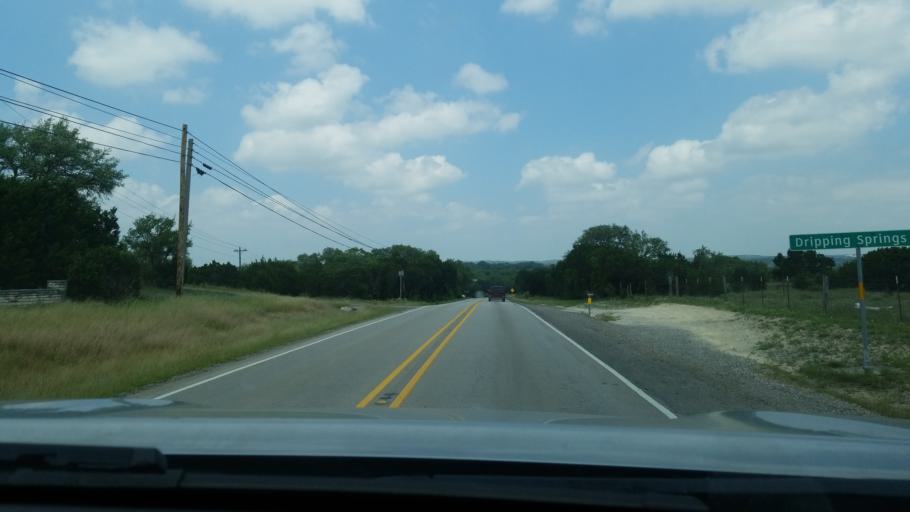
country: US
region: Texas
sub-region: Hays County
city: Dripping Springs
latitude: 30.1330
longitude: -98.0321
